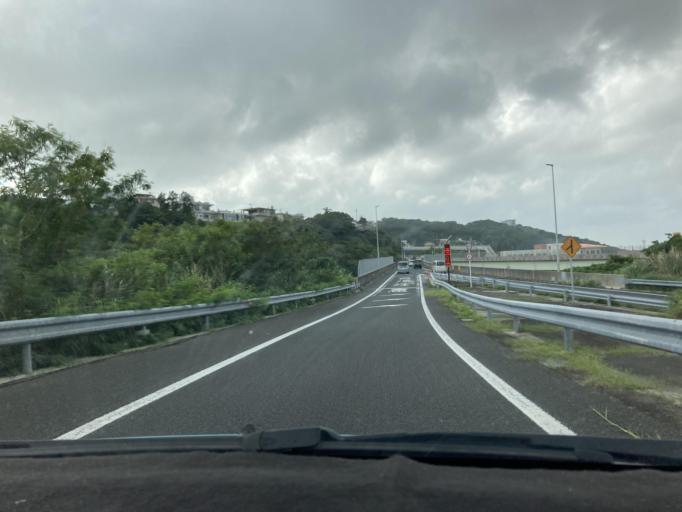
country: JP
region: Okinawa
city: Tomigusuku
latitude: 26.1718
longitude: 127.6970
